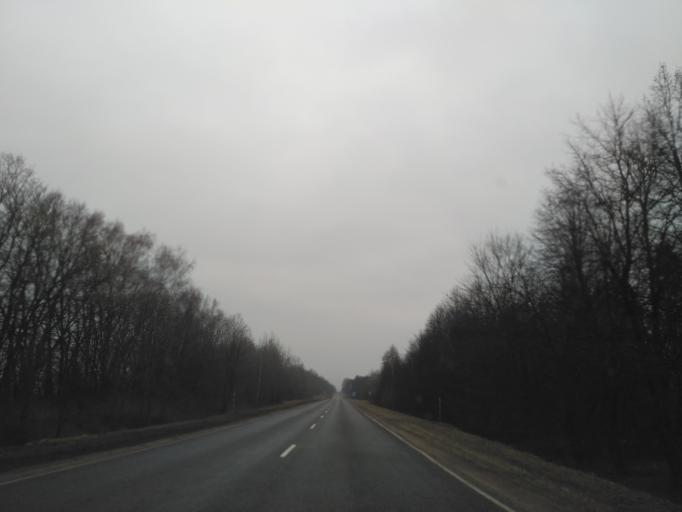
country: BY
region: Minsk
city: Snow
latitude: 53.3021
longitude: 26.4004
